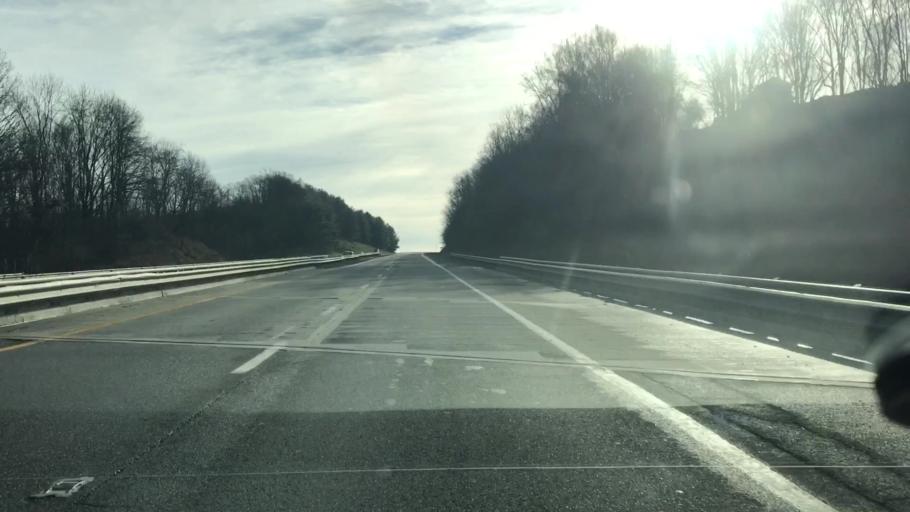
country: US
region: Virginia
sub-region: Montgomery County
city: Christiansburg
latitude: 37.1419
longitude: -80.3861
